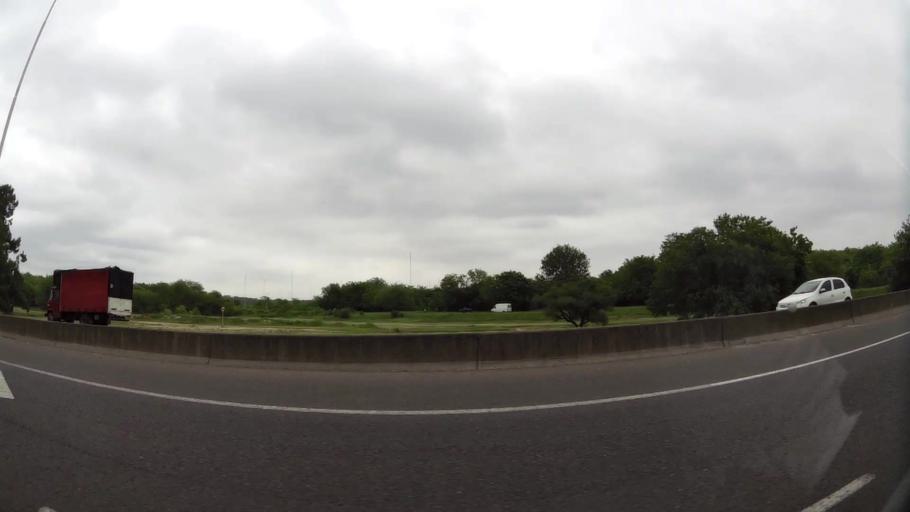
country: AR
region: Buenos Aires
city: San Justo
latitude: -34.7519
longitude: -58.5228
